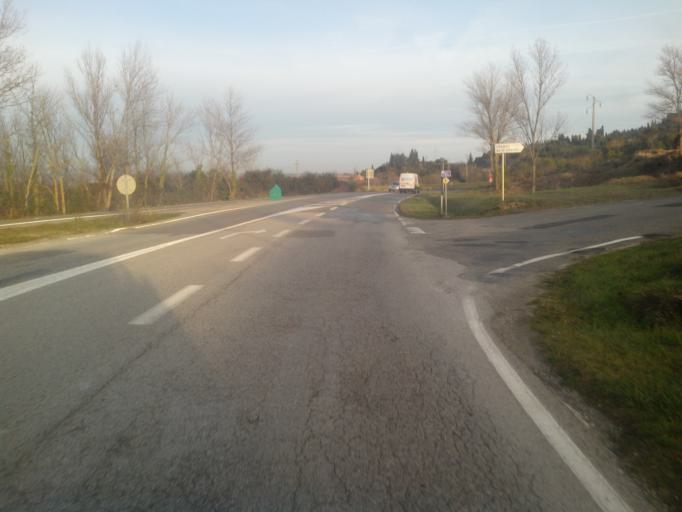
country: FR
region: Languedoc-Roussillon
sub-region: Departement de l'Aude
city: Cazilhac
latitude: 43.2034
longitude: 2.3745
